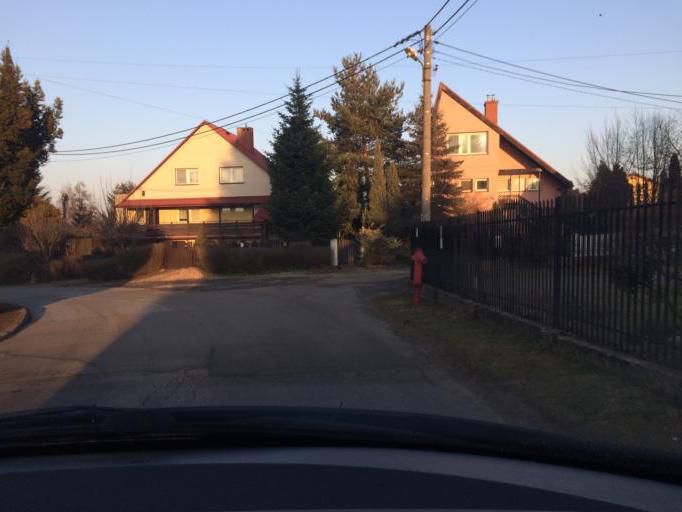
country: PL
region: Lesser Poland Voivodeship
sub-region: Powiat wielicki
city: Czarnochowice
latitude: 50.0083
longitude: 20.0404
